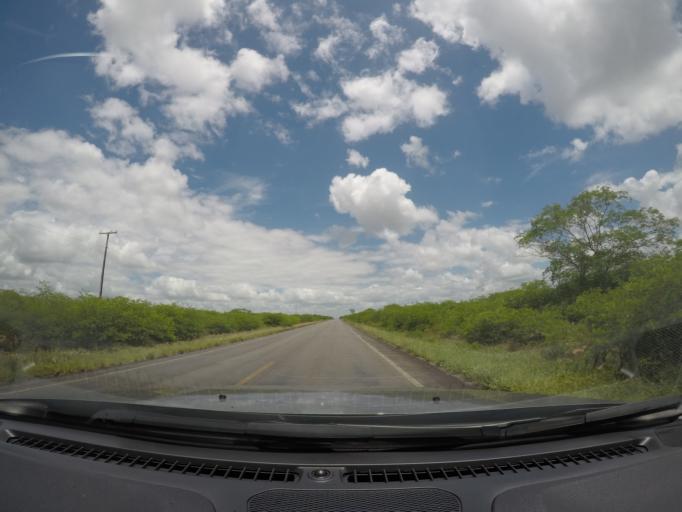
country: BR
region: Bahia
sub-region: Ipira
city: Ipira
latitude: -12.3479
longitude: -39.9988
